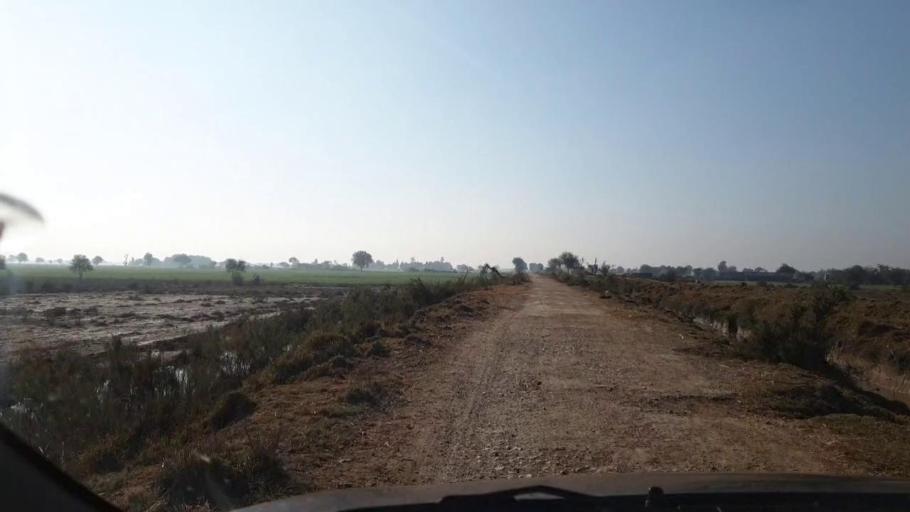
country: PK
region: Sindh
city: Sinjhoro
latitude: 26.0175
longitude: 68.8056
